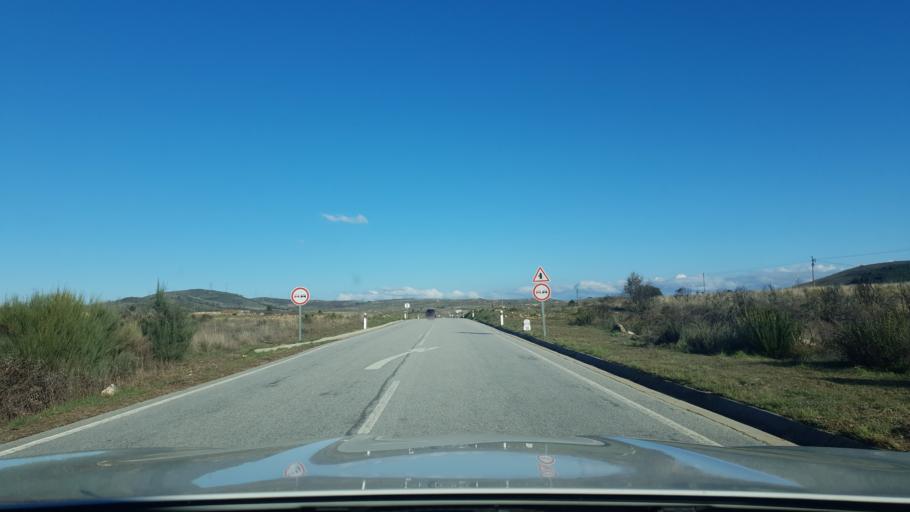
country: PT
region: Braganca
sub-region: Freixo de Espada A Cinta
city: Freixo de Espada a Cinta
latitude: 41.1846
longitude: -6.8302
